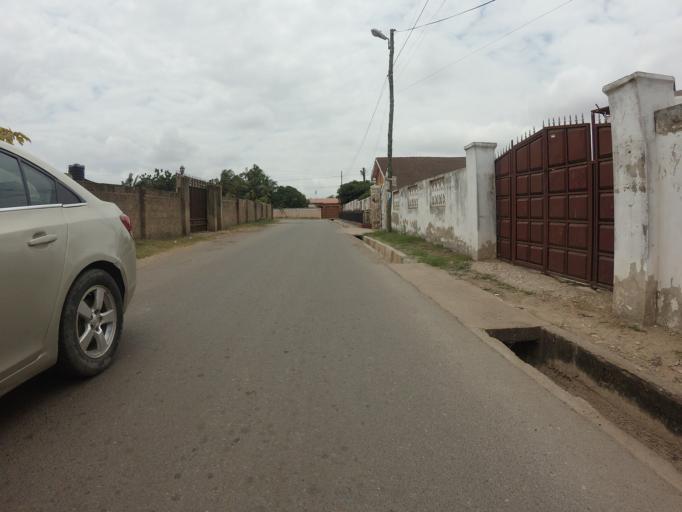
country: GH
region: Greater Accra
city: Teshi Old Town
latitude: 5.6053
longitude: -0.1007
